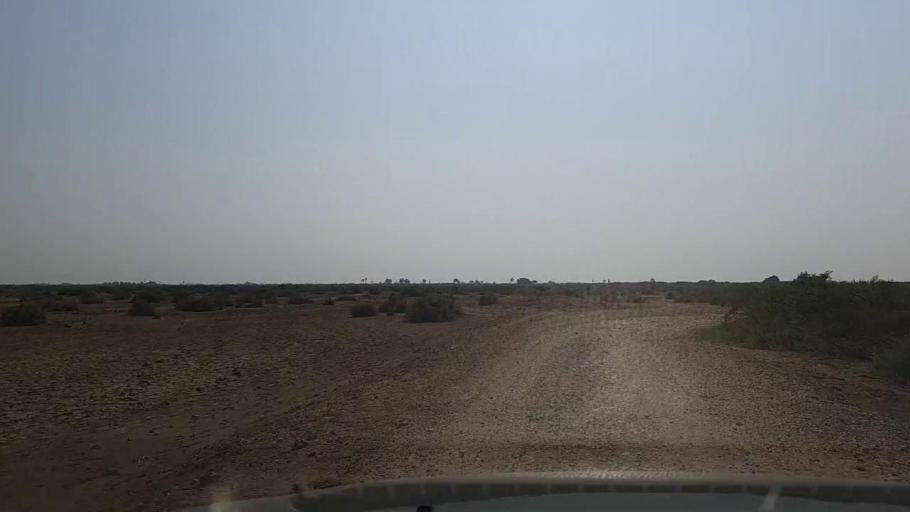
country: PK
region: Sindh
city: Mirpur Sakro
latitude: 24.4269
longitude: 67.7183
